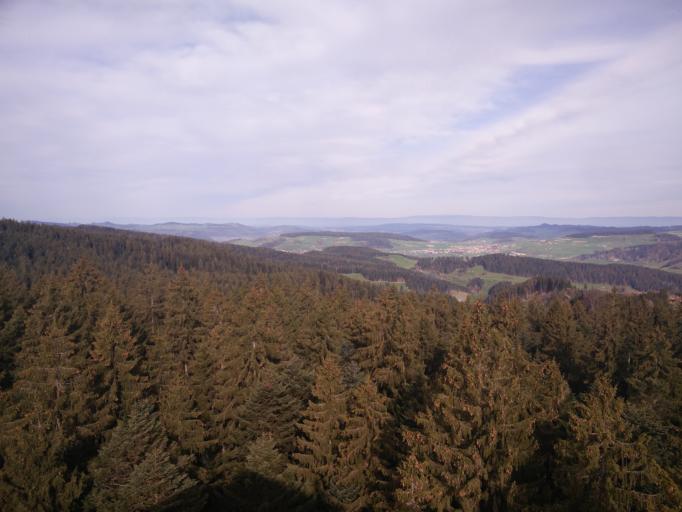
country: CH
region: Bern
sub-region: Bern-Mittelland District
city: Bowil
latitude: 46.8686
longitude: 7.7184
